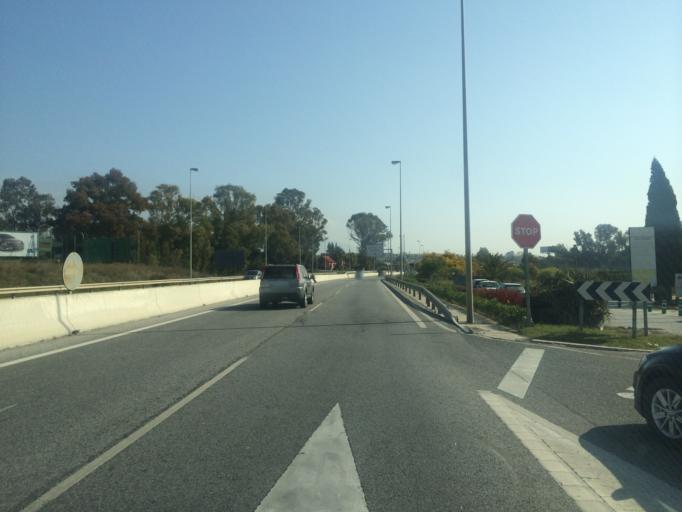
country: ES
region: Andalusia
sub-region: Provincia de Malaga
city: Estepona
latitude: 36.4521
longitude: -5.0822
